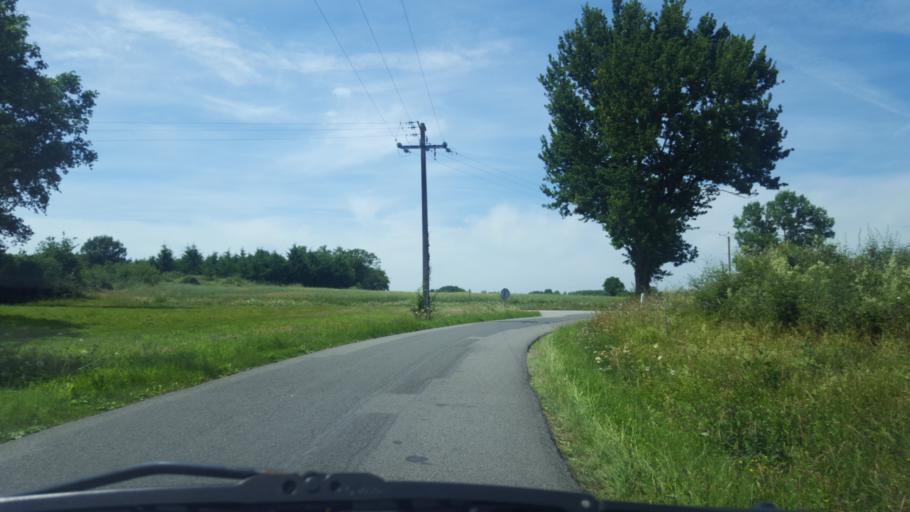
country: FR
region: Pays de la Loire
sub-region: Departement de la Loire-Atlantique
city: La Limouziniere
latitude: 47.0252
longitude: -1.5969
